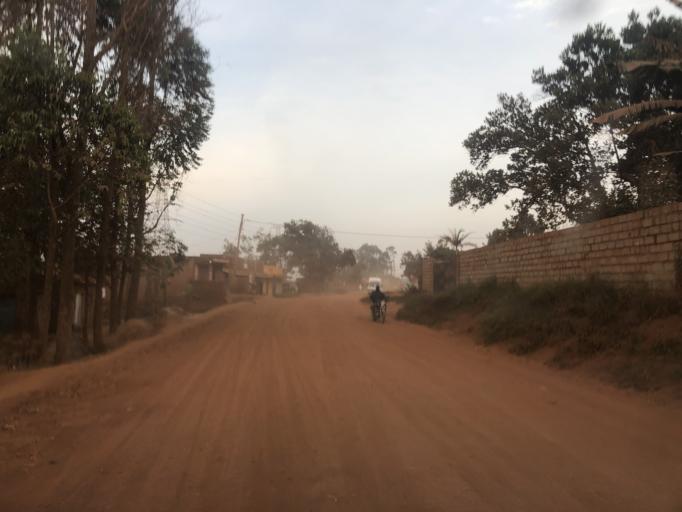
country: UG
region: Central Region
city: Kampala Central Division
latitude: 0.3000
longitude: 32.5156
